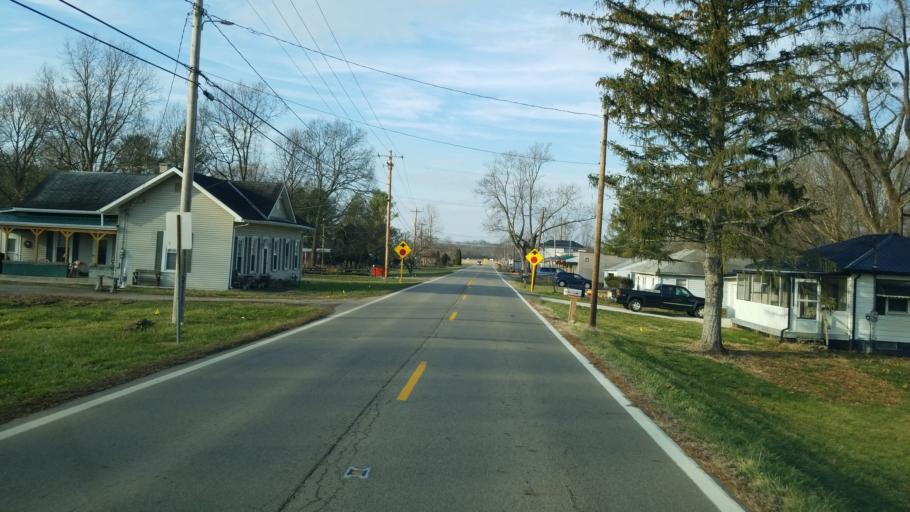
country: US
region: Ohio
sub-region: Ross County
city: Kingston
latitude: 39.4262
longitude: -82.9507
